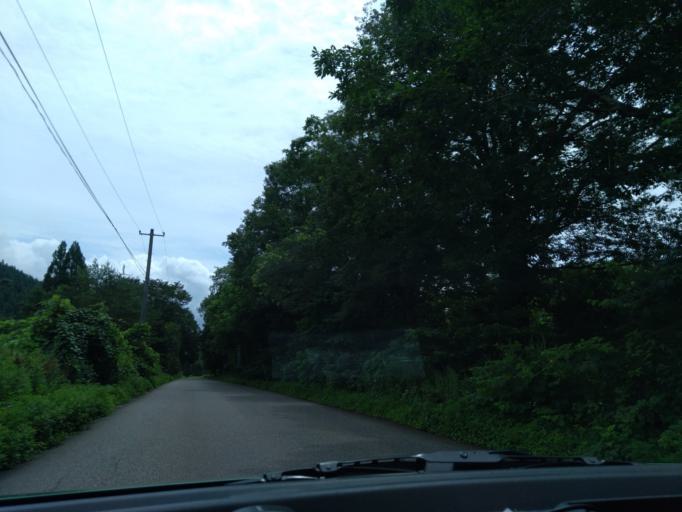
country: JP
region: Akita
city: Kakunodatemachi
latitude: 39.5745
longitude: 140.6301
